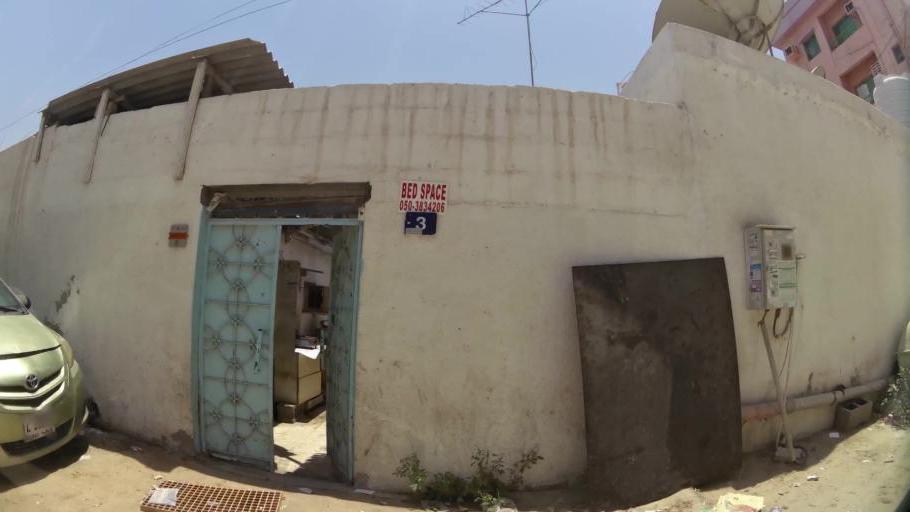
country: AE
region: Ajman
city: Ajman
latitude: 25.4102
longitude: 55.4419
